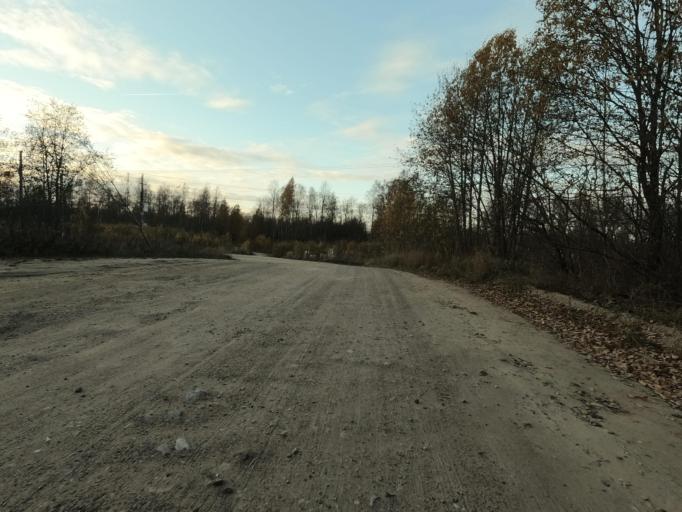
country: RU
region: Leningrad
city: Mga
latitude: 59.7742
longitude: 31.2254
